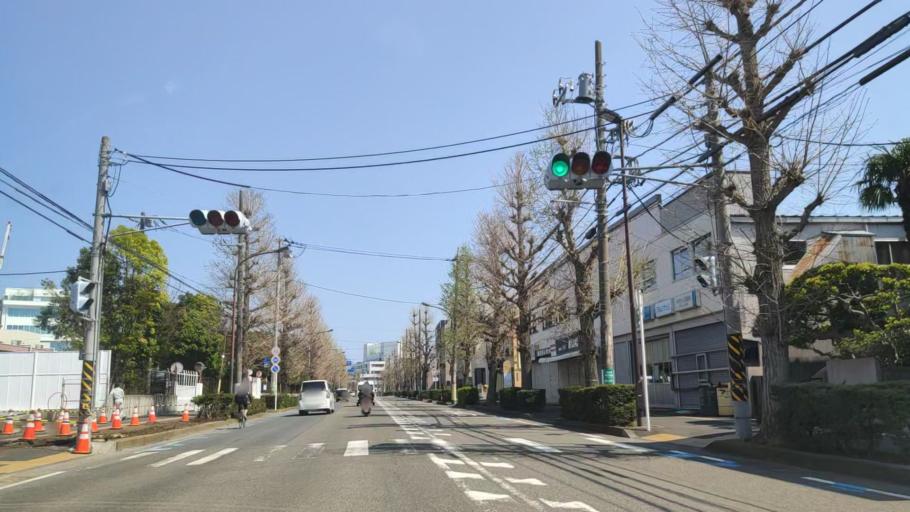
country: JP
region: Kanagawa
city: Hiratsuka
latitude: 35.3358
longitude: 139.3412
